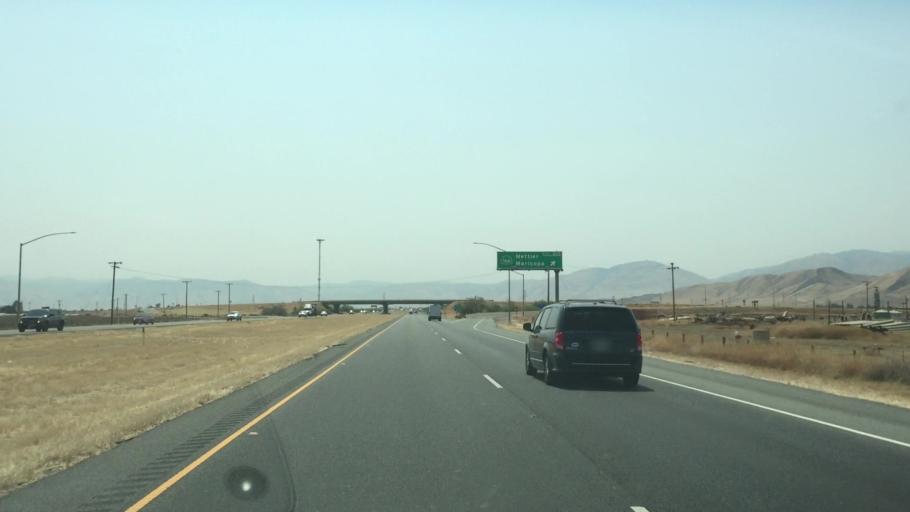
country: US
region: California
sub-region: Kern County
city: Weedpatch
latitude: 35.0630
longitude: -119.0033
